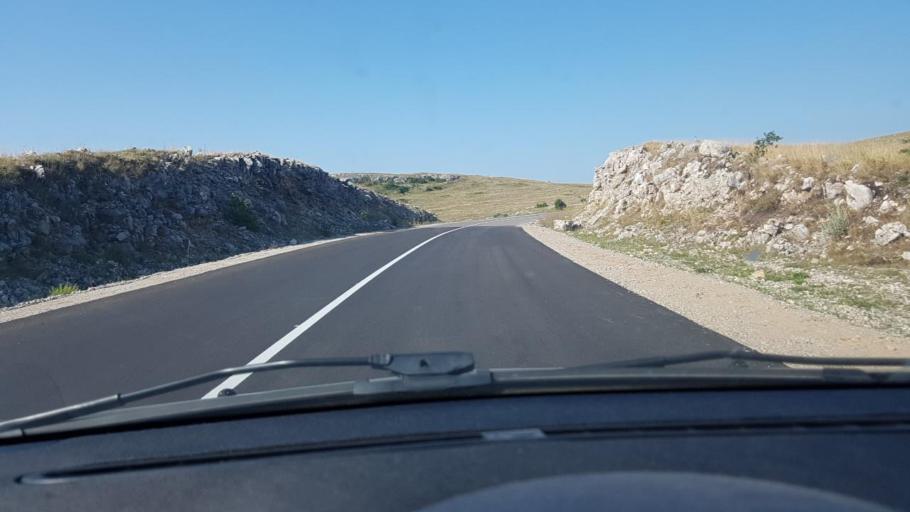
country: BA
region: Federation of Bosnia and Herzegovina
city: Tomislavgrad
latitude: 43.7915
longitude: 17.2554
